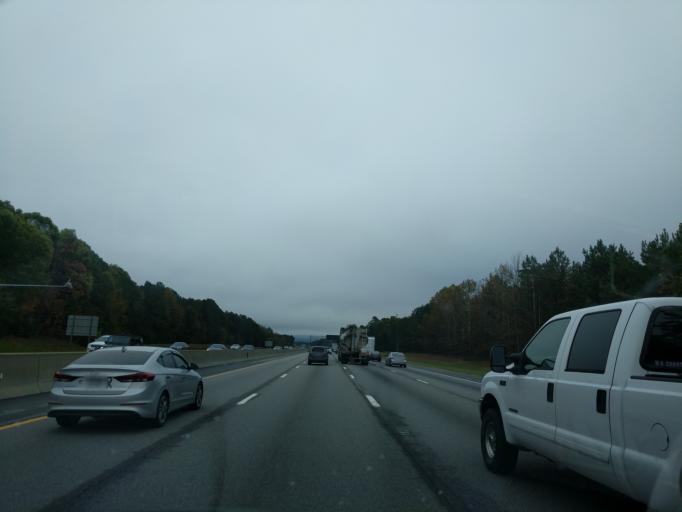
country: US
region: North Carolina
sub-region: Alamance County
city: Mebane
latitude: 36.0754
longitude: -79.1932
